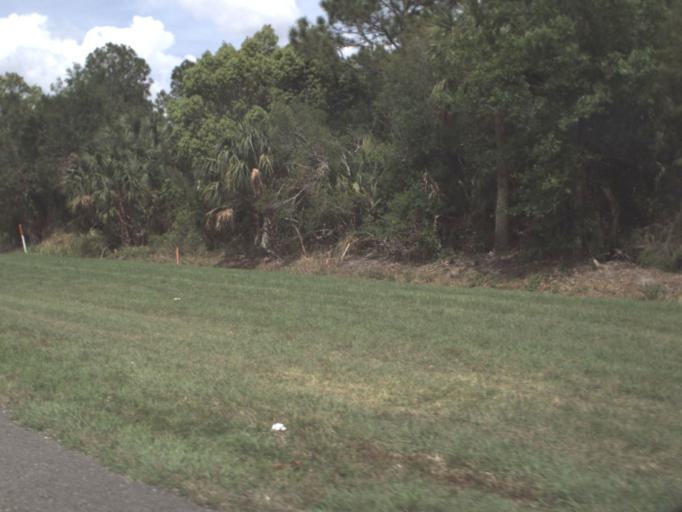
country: US
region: Florida
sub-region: Flagler County
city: Bunnell
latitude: 29.3406
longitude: -81.3109
